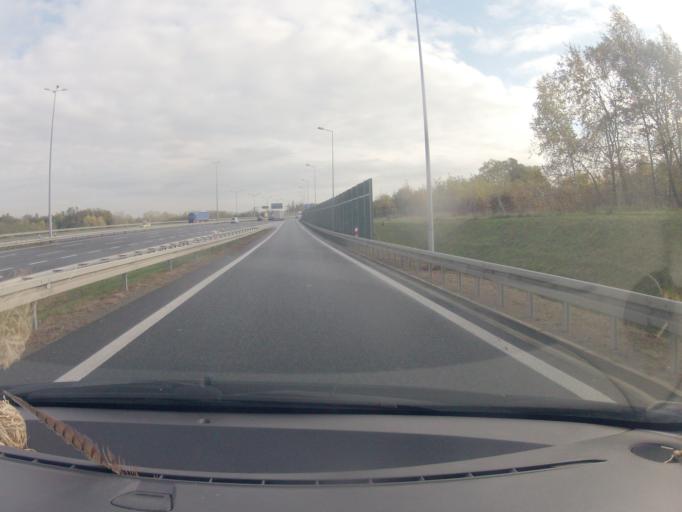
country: PL
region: Lesser Poland Voivodeship
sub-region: Powiat wielicki
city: Czarnochowice
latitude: 50.0054
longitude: 20.0259
